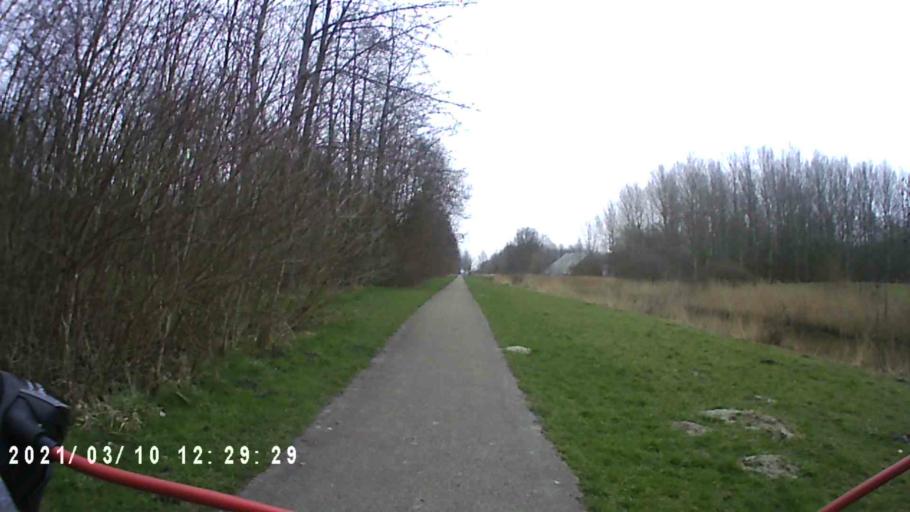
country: NL
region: Groningen
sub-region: Gemeente Groningen
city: Oosterpark
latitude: 53.2520
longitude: 6.6194
